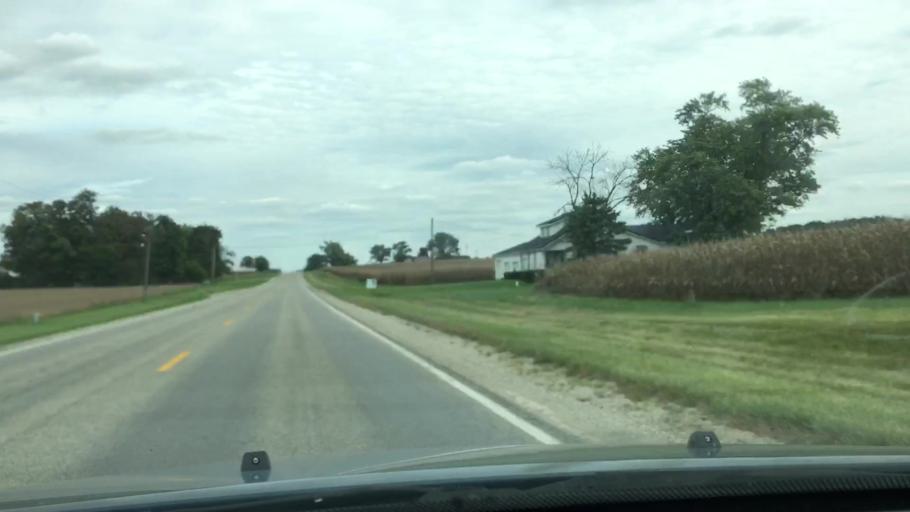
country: US
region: Indiana
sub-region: Adams County
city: Geneva
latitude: 40.5419
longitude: -84.9077
